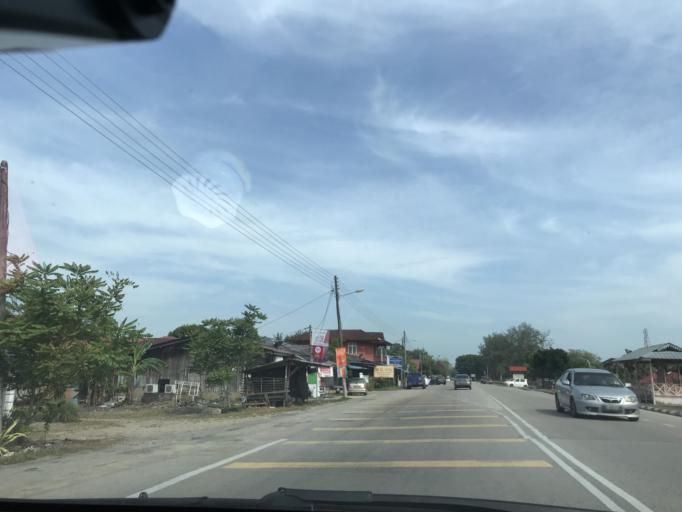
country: MY
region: Kelantan
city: Tumpat
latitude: 6.1891
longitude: 102.1581
